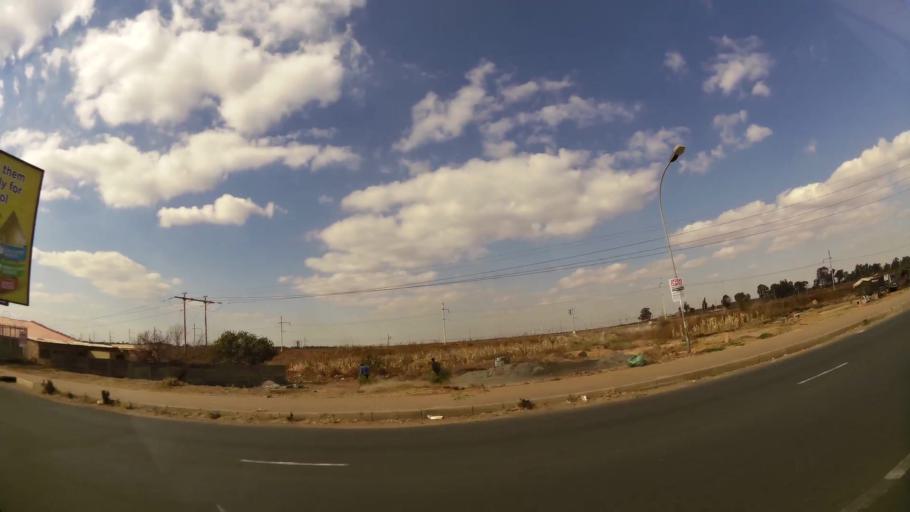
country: ZA
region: Gauteng
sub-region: Ekurhuleni Metropolitan Municipality
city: Tembisa
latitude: -25.9947
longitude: 28.2454
